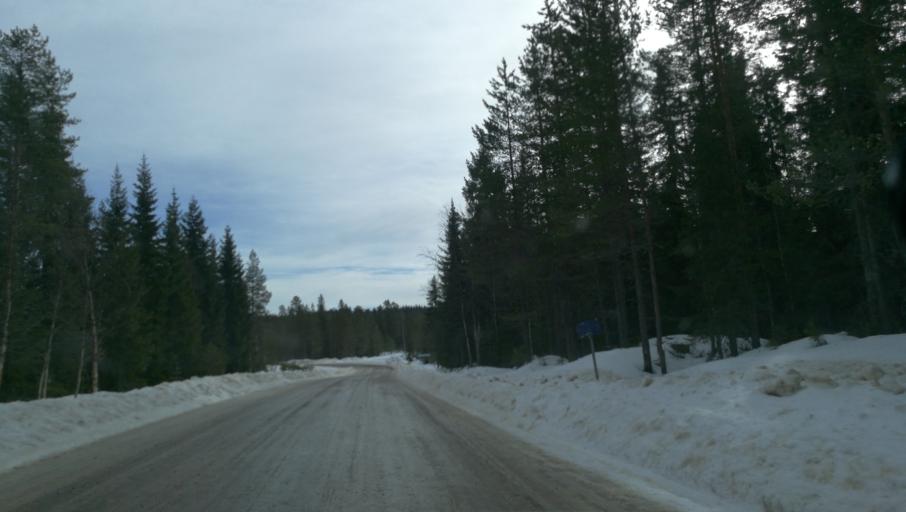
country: SE
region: Vaermland
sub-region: Torsby Kommun
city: Torsby
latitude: 60.6495
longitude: 12.8954
